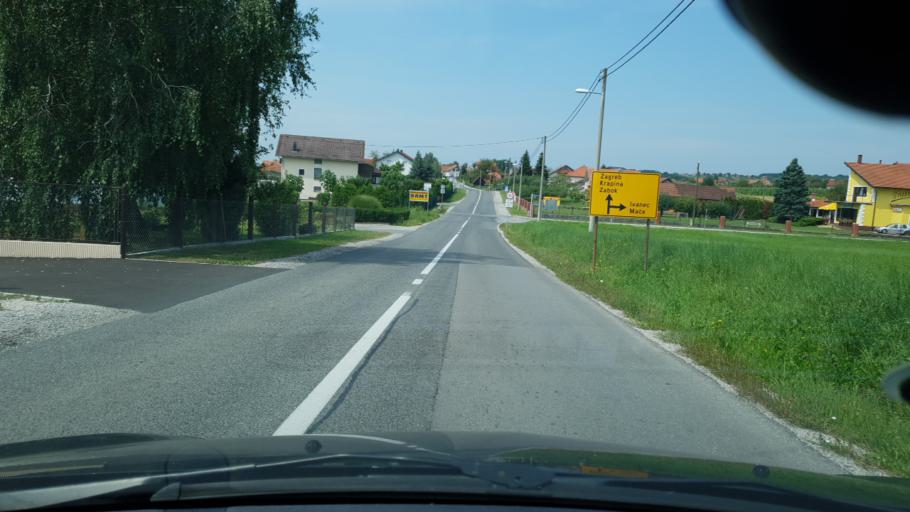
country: HR
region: Krapinsko-Zagorska
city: Selnica
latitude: 46.0526
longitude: 16.0396
